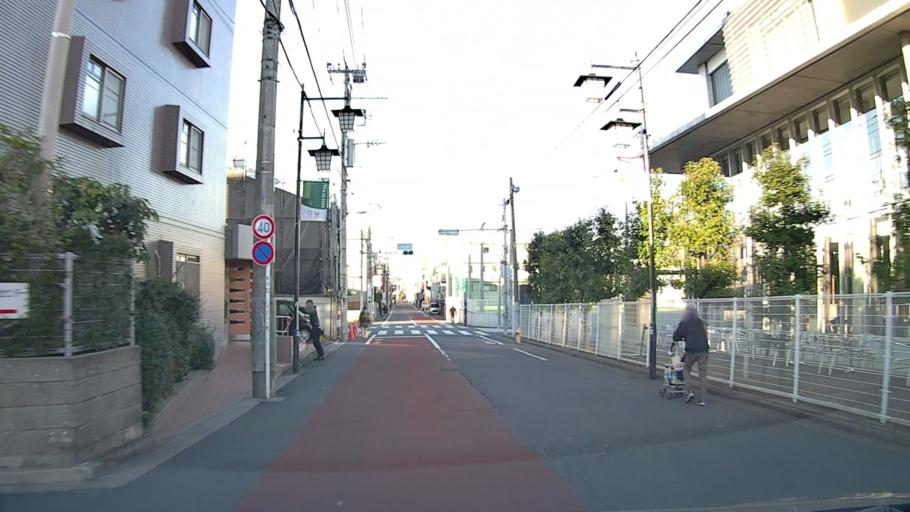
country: JP
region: Tokyo
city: Tokyo
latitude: 35.7247
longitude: 139.6627
